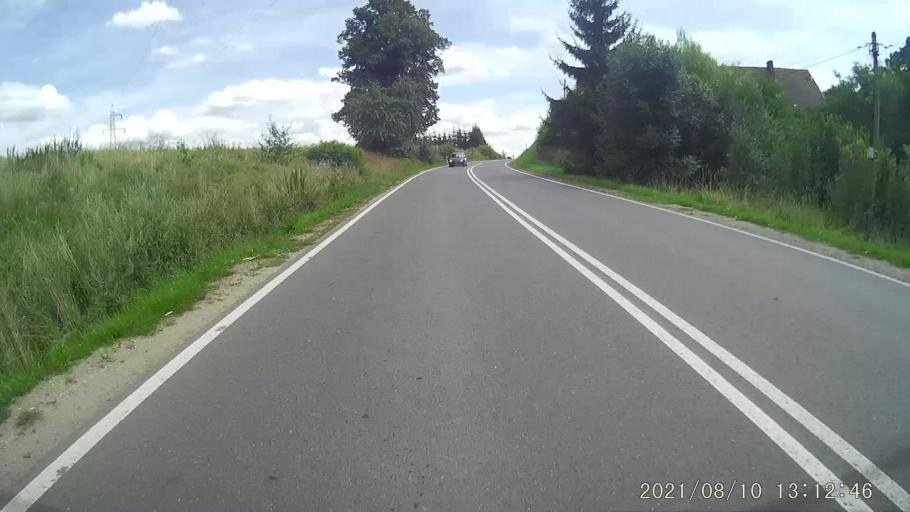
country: PL
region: Lower Silesian Voivodeship
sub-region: Powiat klodzki
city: Nowa Ruda
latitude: 50.5173
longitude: 16.5094
